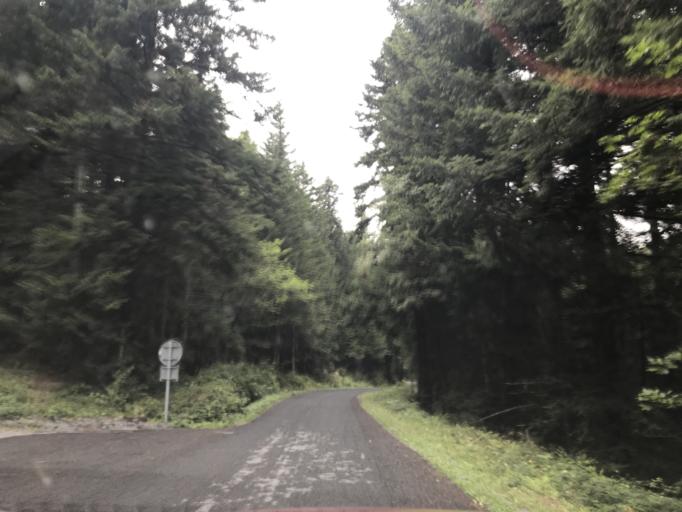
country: FR
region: Auvergne
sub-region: Departement du Puy-de-Dome
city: Job
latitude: 45.6591
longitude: 3.7737
